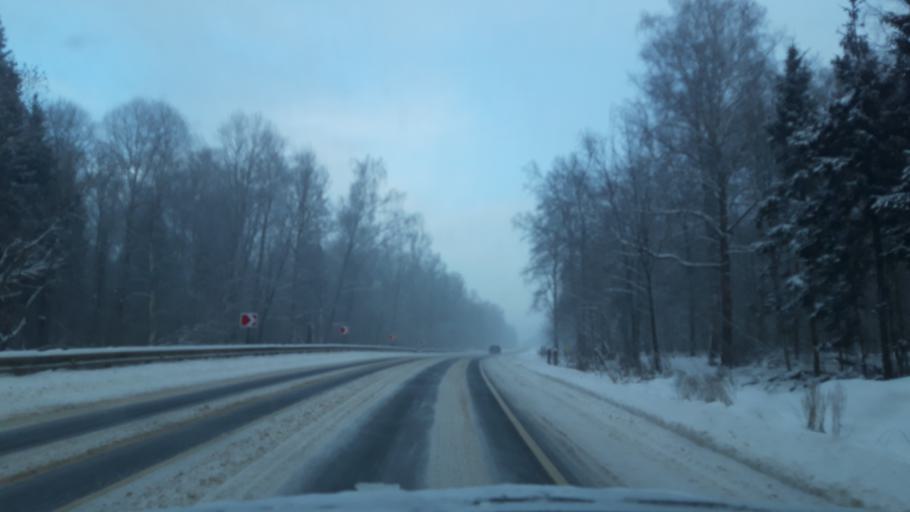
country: RU
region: Moskovskaya
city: Gorshkovo
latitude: 56.2927
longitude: 37.3981
